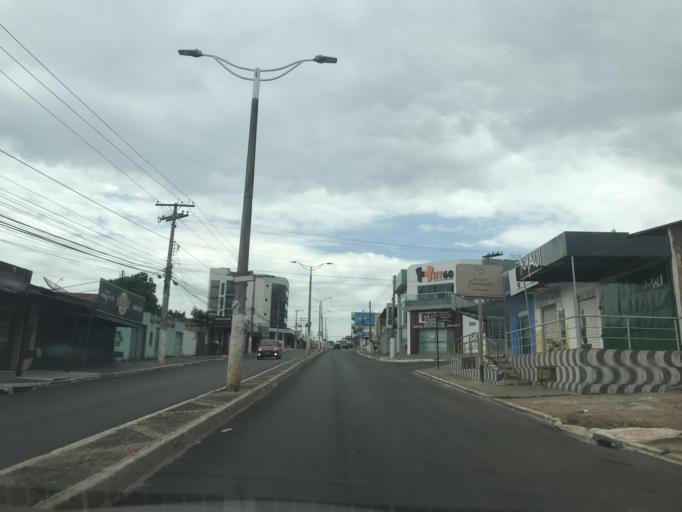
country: BR
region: Goias
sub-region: Luziania
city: Luziania
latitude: -16.2514
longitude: -47.9552
